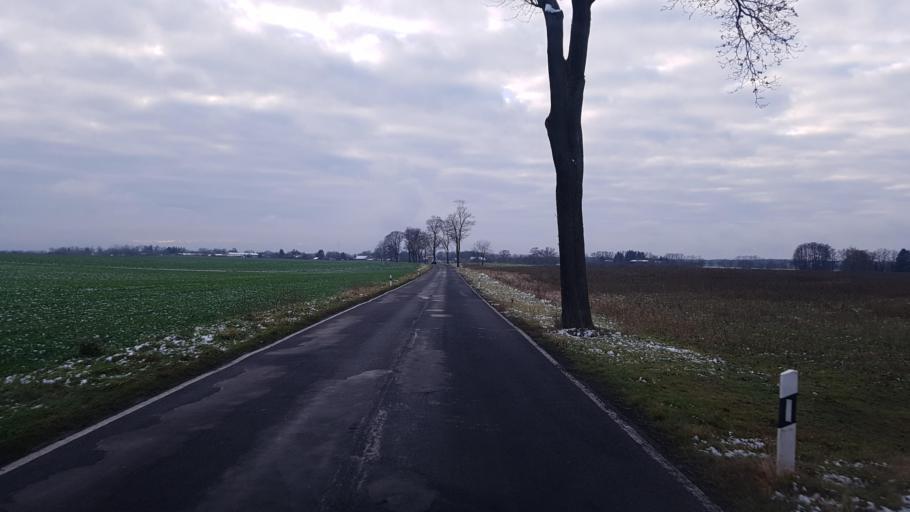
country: DE
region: Brandenburg
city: Rehfelde
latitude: 52.5219
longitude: 13.9105
